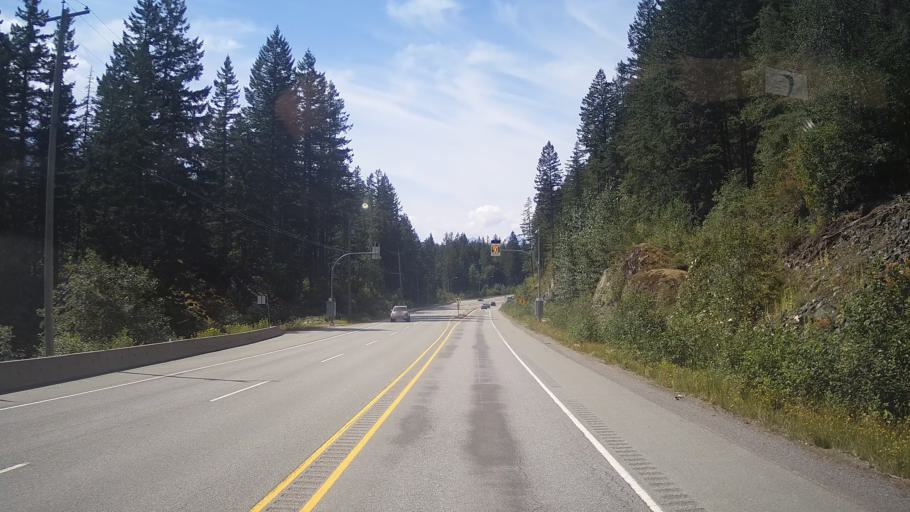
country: CA
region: British Columbia
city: Whistler
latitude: 50.0130
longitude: -123.1244
